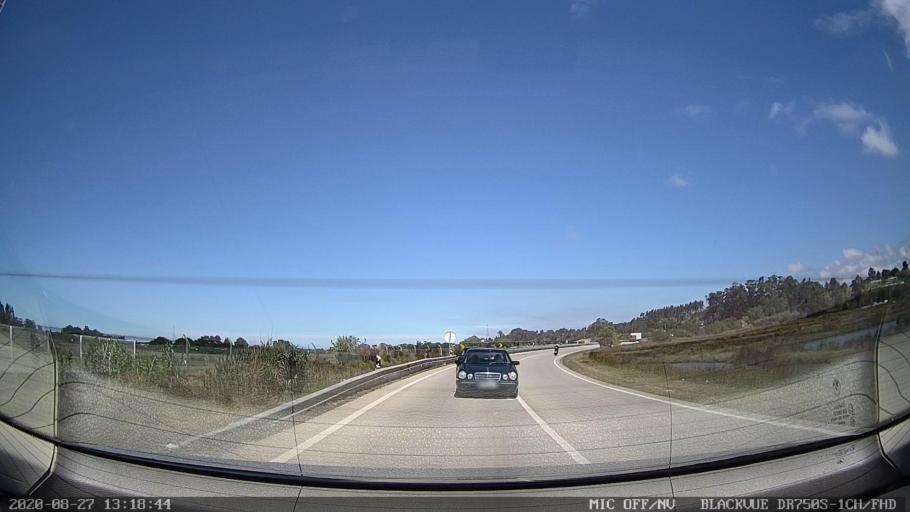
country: PT
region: Aveiro
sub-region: Vagos
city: Vagos
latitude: 40.5716
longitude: -8.6827
